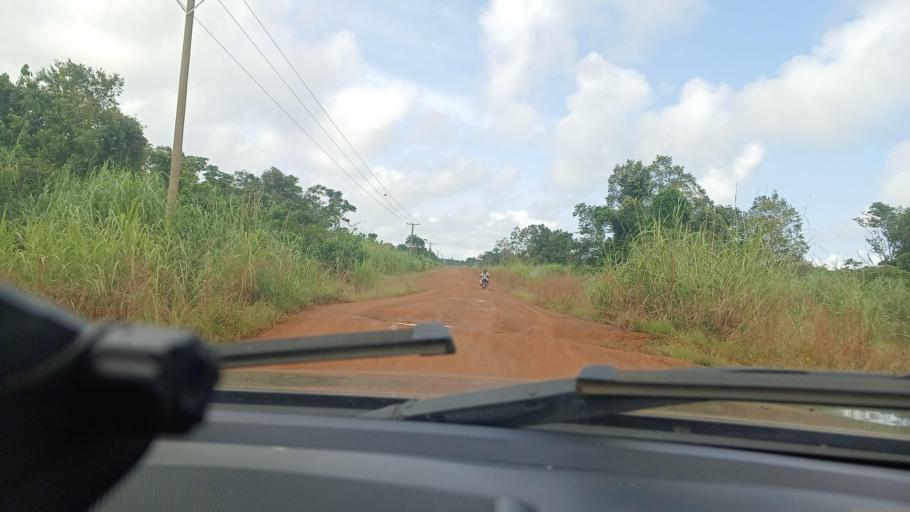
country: LR
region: Grand Cape Mount
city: Robertsport
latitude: 6.6842
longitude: -11.1263
